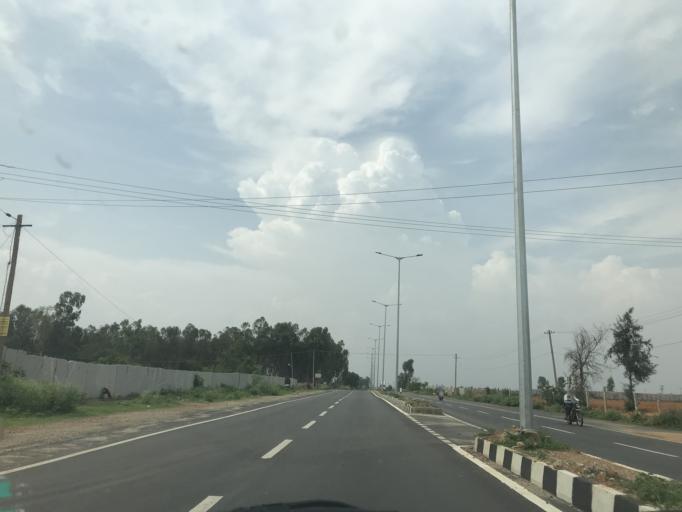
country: IN
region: Karnataka
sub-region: Bangalore Urban
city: Yelahanka
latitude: 13.1133
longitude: 77.6674
